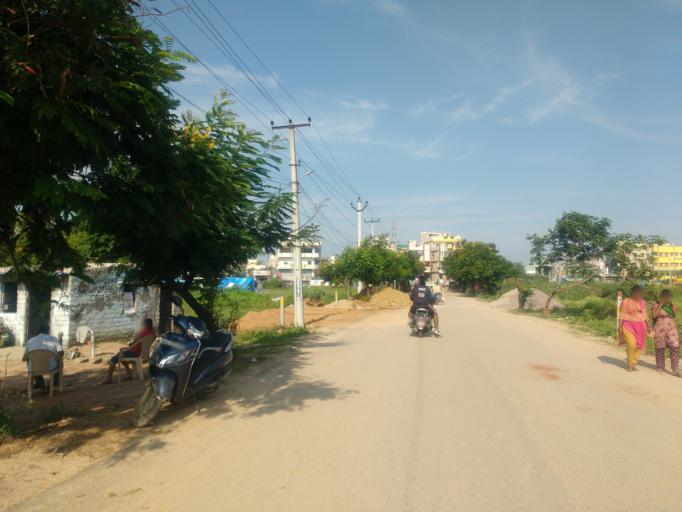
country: IN
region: Telangana
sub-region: Medak
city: Patancheru
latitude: 17.5317
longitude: 78.2998
